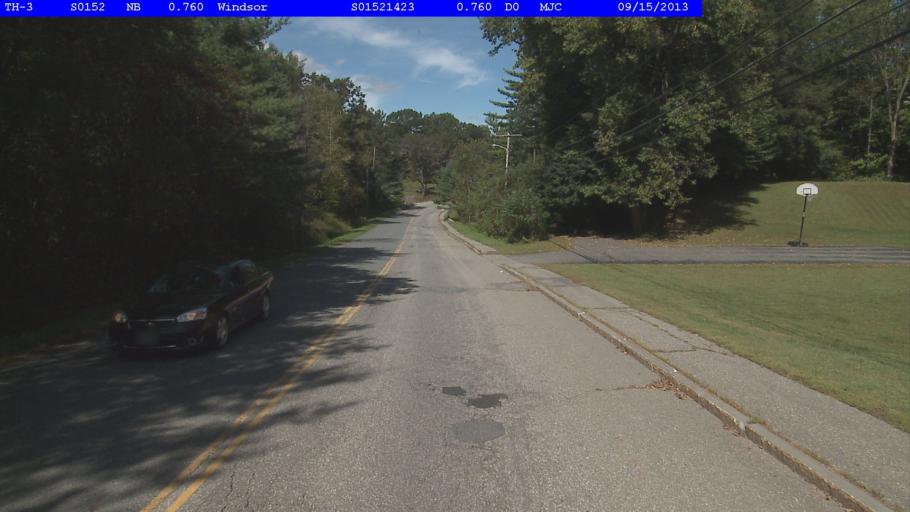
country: US
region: Vermont
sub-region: Windsor County
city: Windsor
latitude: 43.4843
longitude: -72.3997
